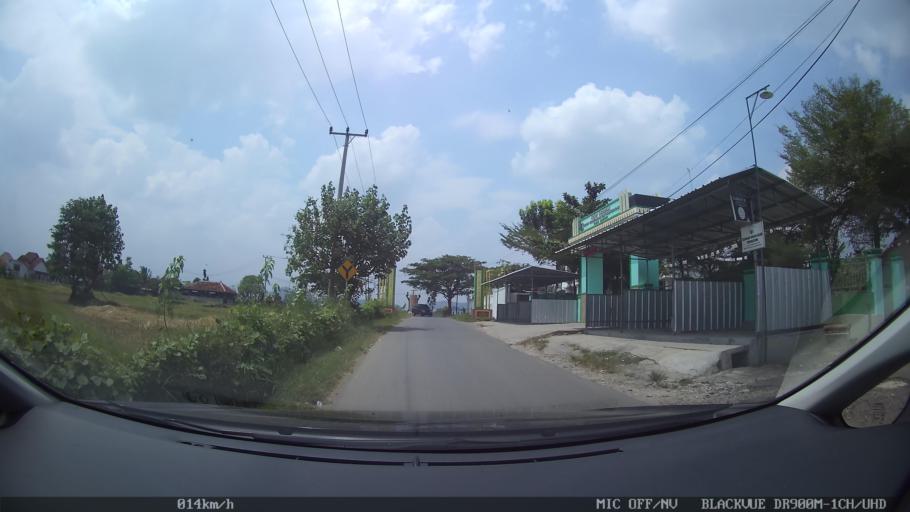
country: ID
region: Lampung
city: Pringsewu
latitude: -5.3521
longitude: 104.9907
